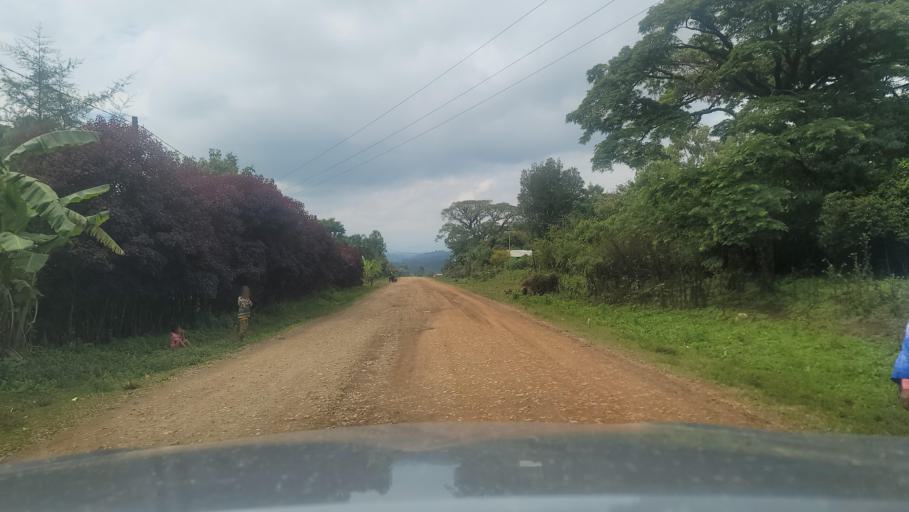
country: ET
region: Oromiya
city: Agaro
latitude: 7.7945
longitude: 36.4475
